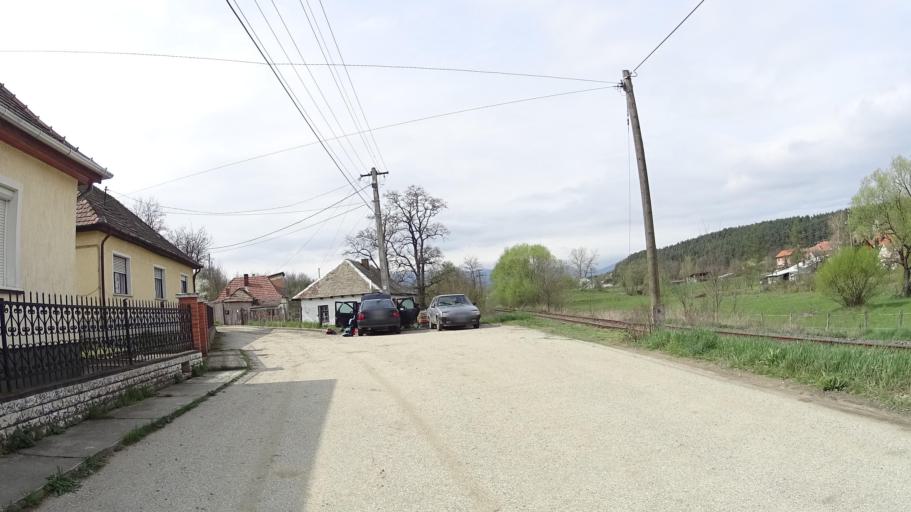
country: HU
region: Nograd
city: Diosjeno
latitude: 47.8874
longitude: 19.0680
